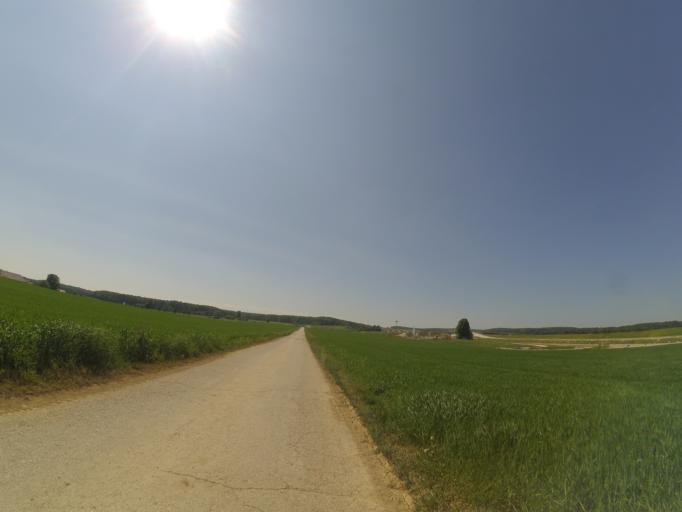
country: DE
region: Baden-Wuerttemberg
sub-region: Tuebingen Region
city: Merklingen
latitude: 48.5169
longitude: 9.7513
